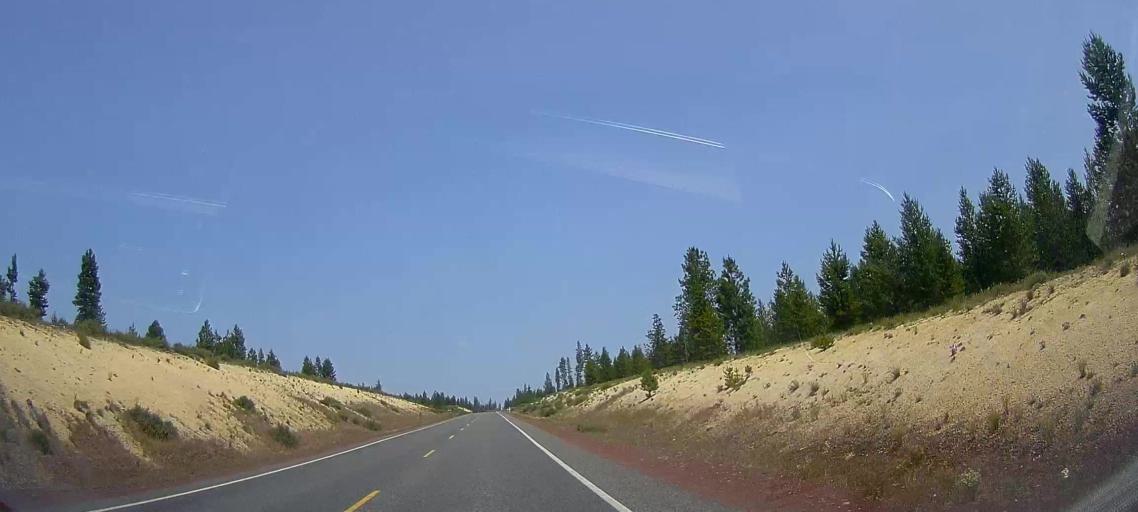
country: US
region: Oregon
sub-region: Deschutes County
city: La Pine
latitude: 43.4017
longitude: -121.7247
